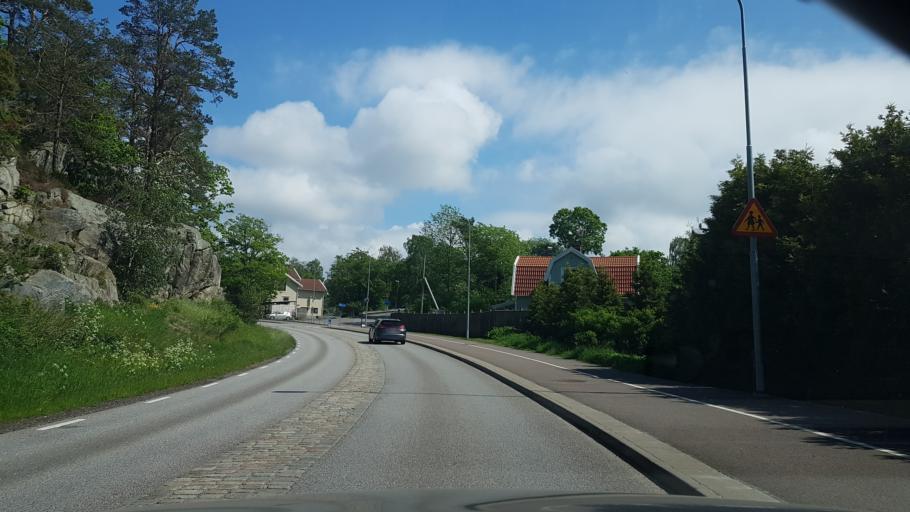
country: SE
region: Vaestra Goetaland
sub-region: Goteborg
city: Billdal
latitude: 57.5994
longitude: 11.9408
